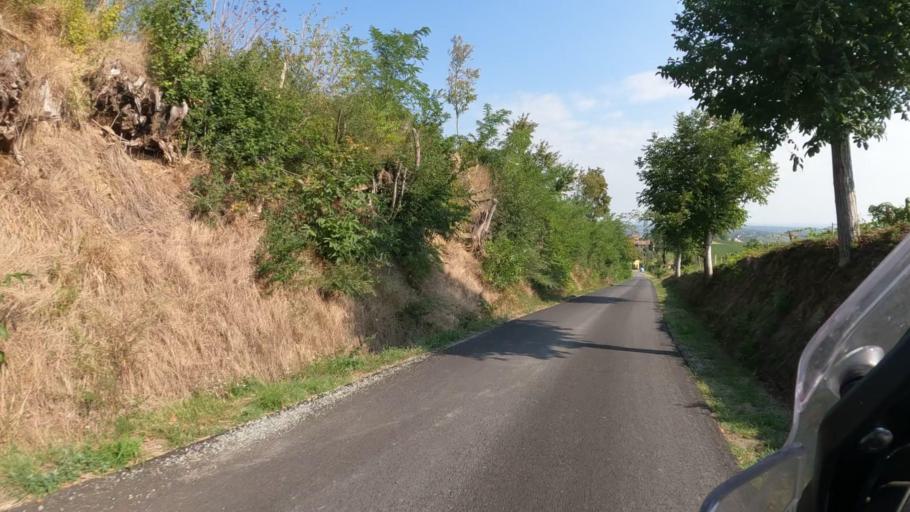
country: IT
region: Piedmont
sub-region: Provincia di Asti
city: Castel Boglione
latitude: 44.7523
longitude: 8.3829
